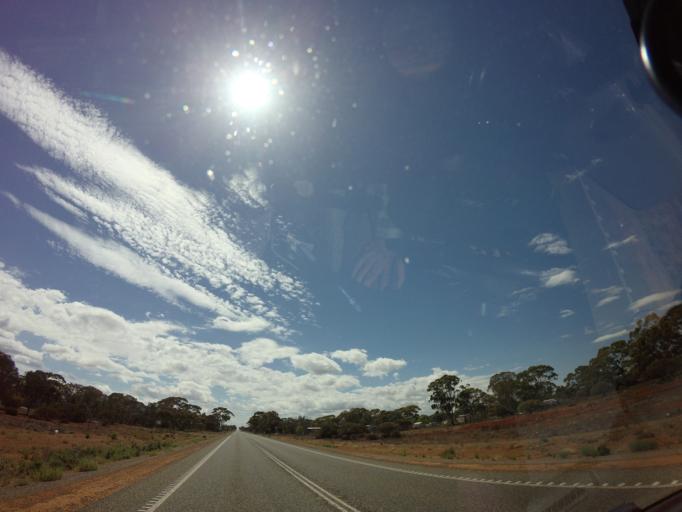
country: AU
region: Western Australia
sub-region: Kalgoorlie/Boulder
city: Boulder
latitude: -30.9546
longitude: 121.1435
